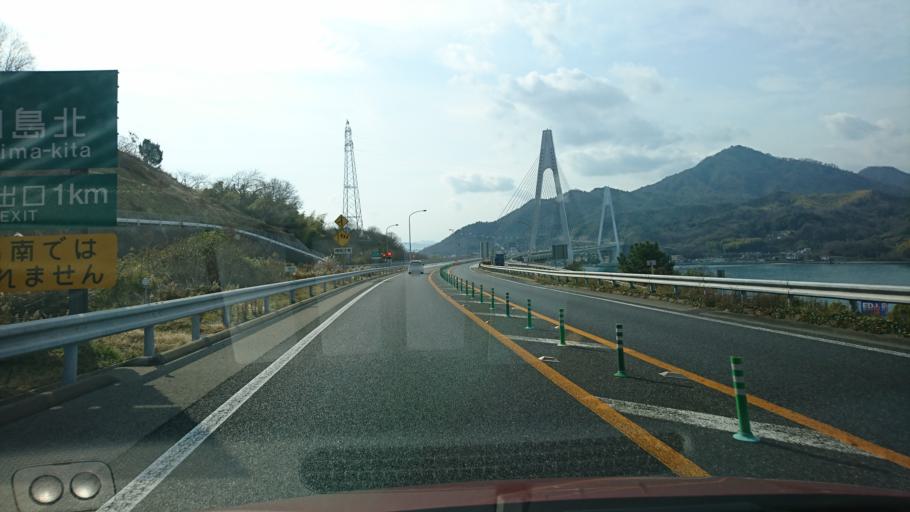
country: JP
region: Hiroshima
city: Innoshima
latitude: 34.3088
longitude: 133.1551
